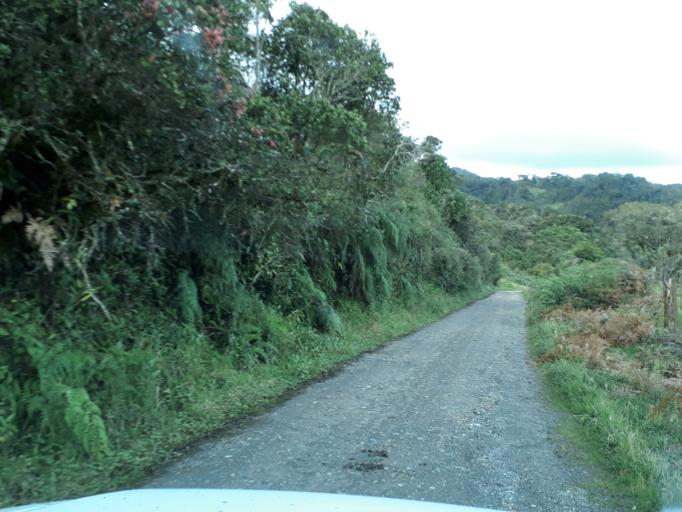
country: CO
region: Cundinamarca
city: Guasca
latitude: 4.8325
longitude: -73.7696
